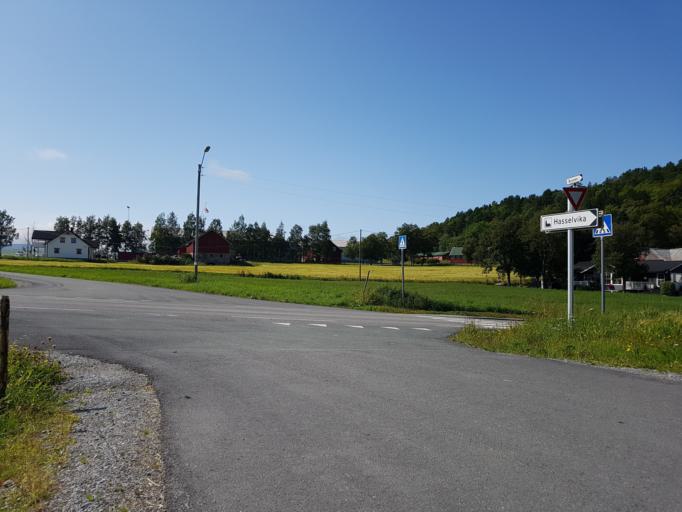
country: NO
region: Sor-Trondelag
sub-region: Agdenes
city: Lensvik
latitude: 63.6291
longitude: 9.8256
